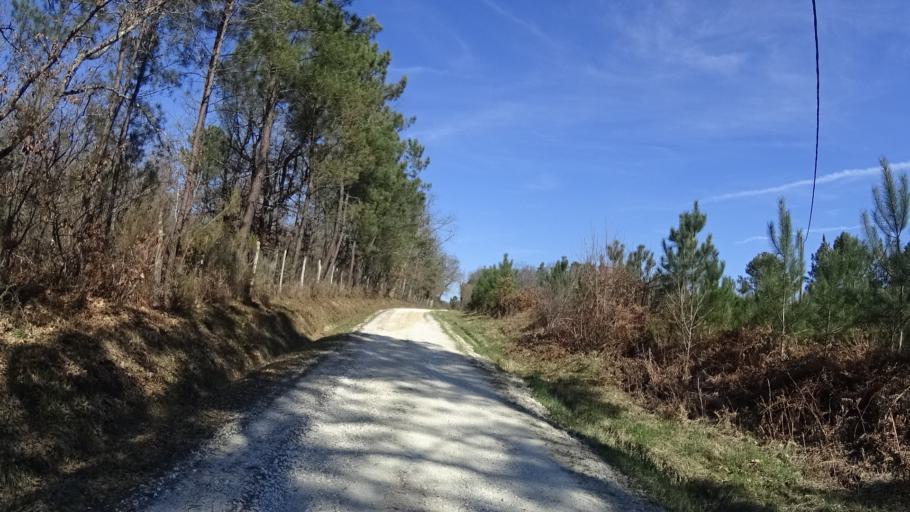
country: FR
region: Aquitaine
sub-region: Departement de la Dordogne
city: Riberac
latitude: 45.2006
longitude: 0.3152
